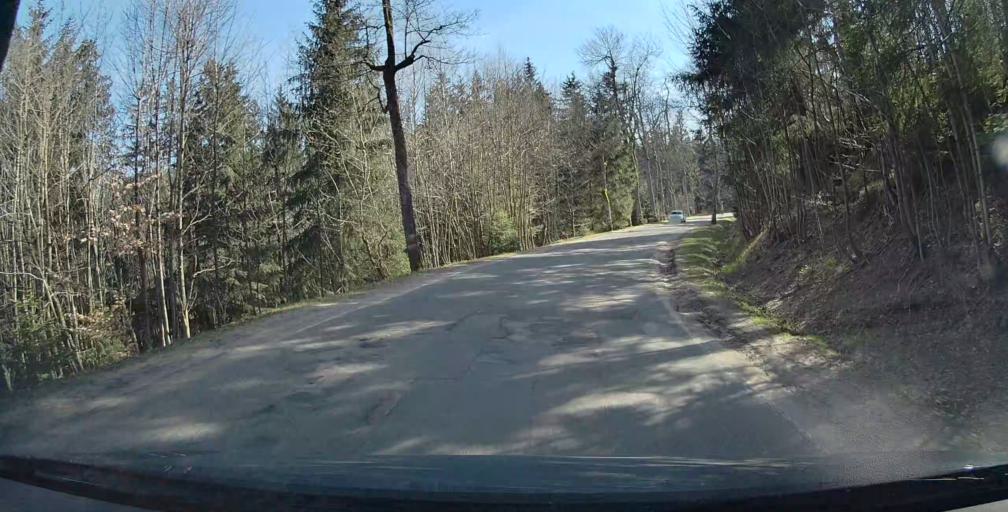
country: PL
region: Lower Silesian Voivodeship
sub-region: Powiat klodzki
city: Radkow
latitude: 50.4631
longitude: 16.3494
